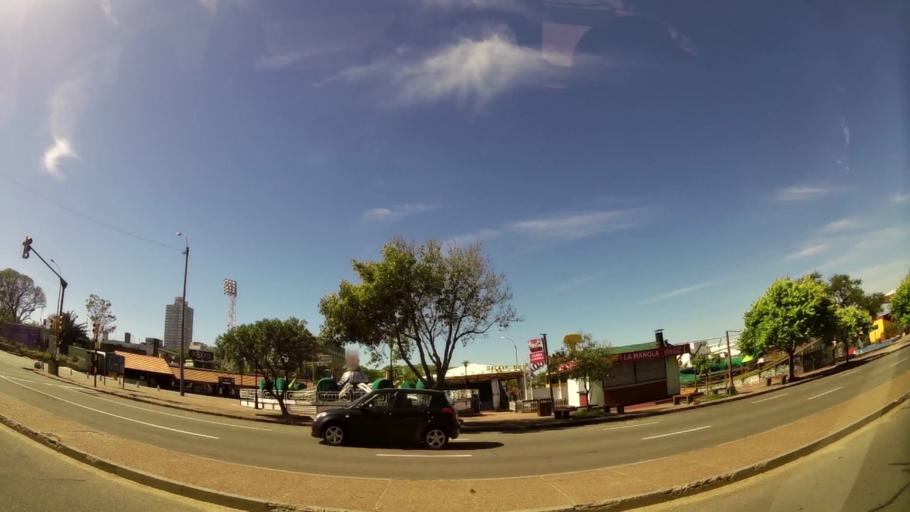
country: UY
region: Montevideo
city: Montevideo
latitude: -34.9154
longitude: -56.1681
